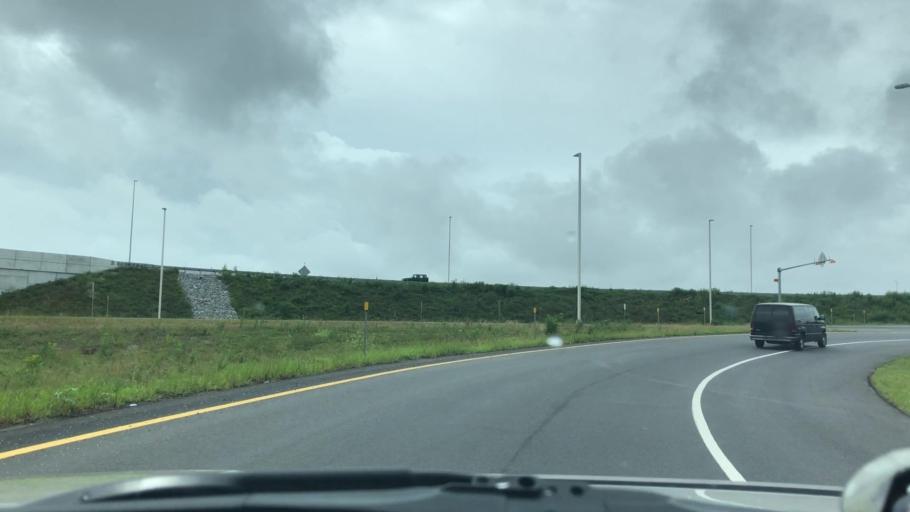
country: US
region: New Jersey
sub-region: Hudson County
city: Bayonne
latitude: 40.6801
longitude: -74.0959
